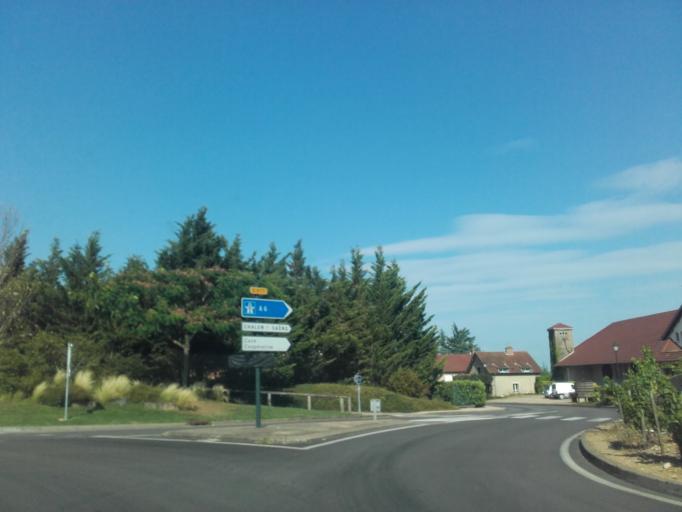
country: FR
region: Bourgogne
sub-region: Departement de Saone-et-Loire
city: Buxy
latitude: 46.7131
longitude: 4.7030
